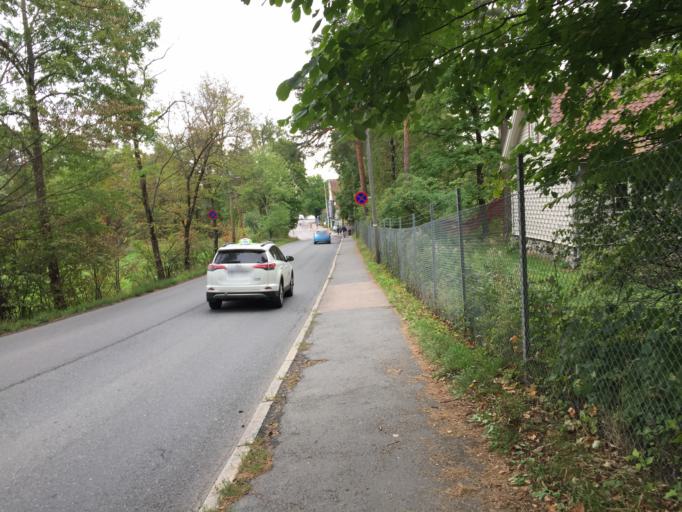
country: NO
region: Oslo
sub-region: Oslo
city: Sjolyststranda
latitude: 59.9086
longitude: 10.6848
